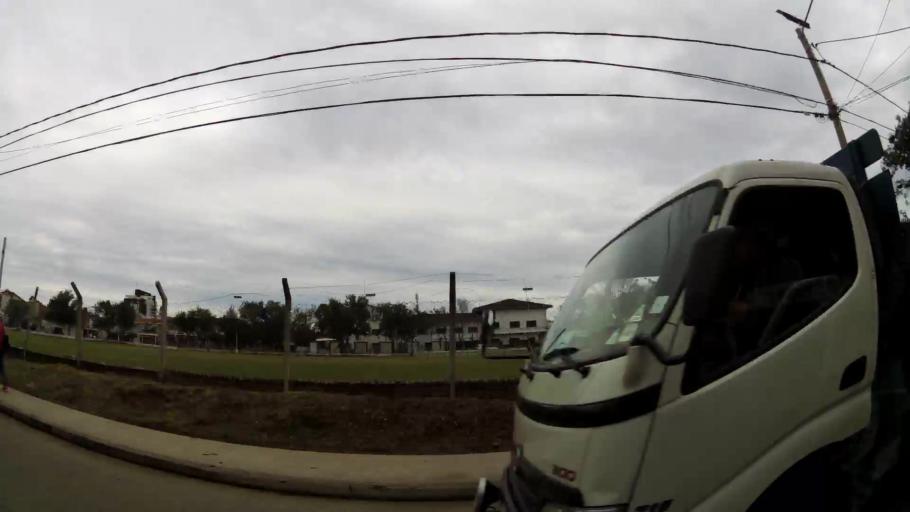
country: BO
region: Santa Cruz
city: Santa Cruz de la Sierra
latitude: -17.7750
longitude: -63.1598
